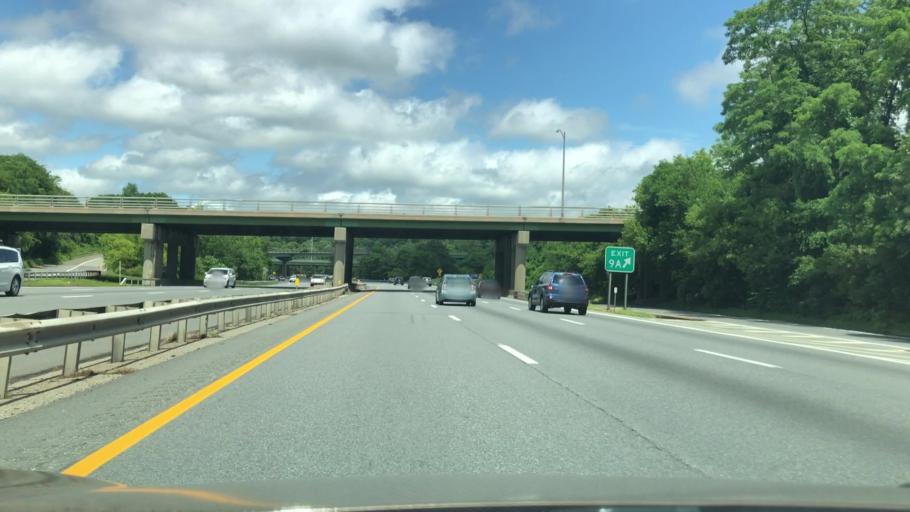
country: US
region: New York
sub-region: Westchester County
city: Purchase
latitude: 41.0220
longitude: -73.7285
